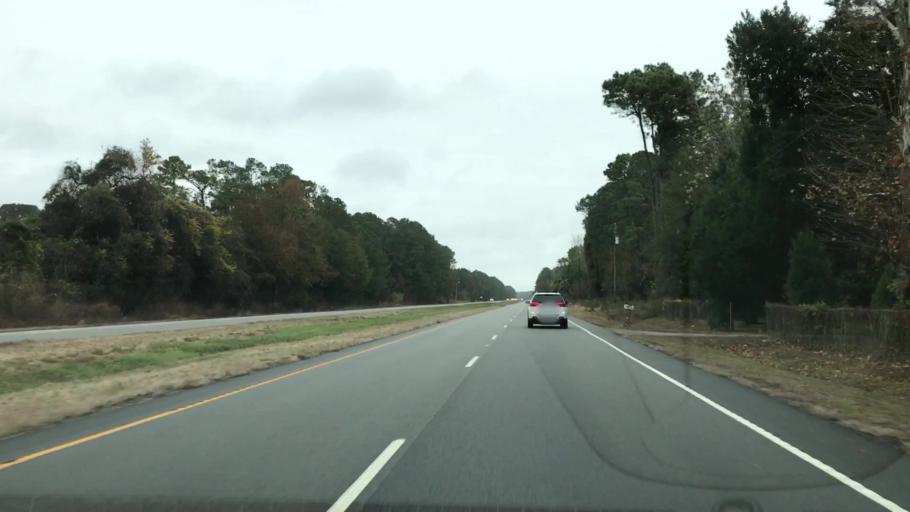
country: US
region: South Carolina
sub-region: Charleston County
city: Awendaw
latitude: 33.1075
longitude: -79.4626
